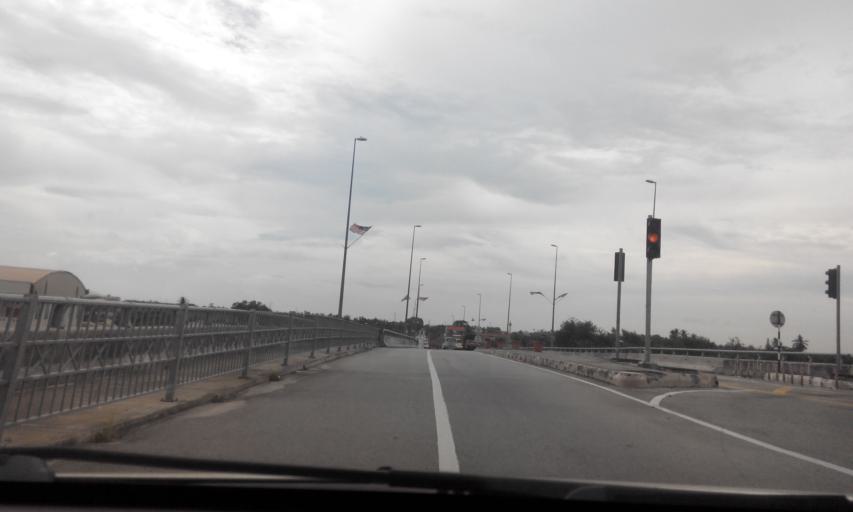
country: MY
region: Perak
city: Parit Buntar
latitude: 5.1321
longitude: 100.4858
